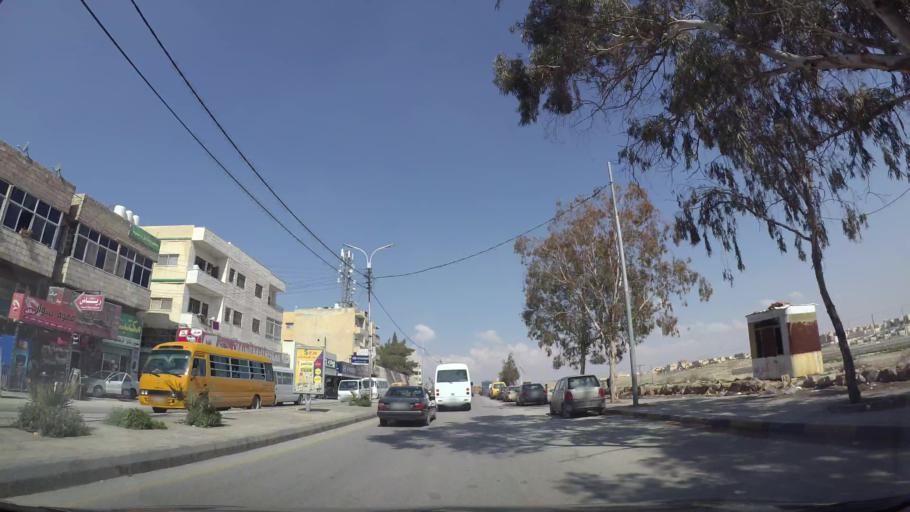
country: JO
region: Zarqa
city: Zarqa
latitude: 32.0770
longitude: 36.1024
